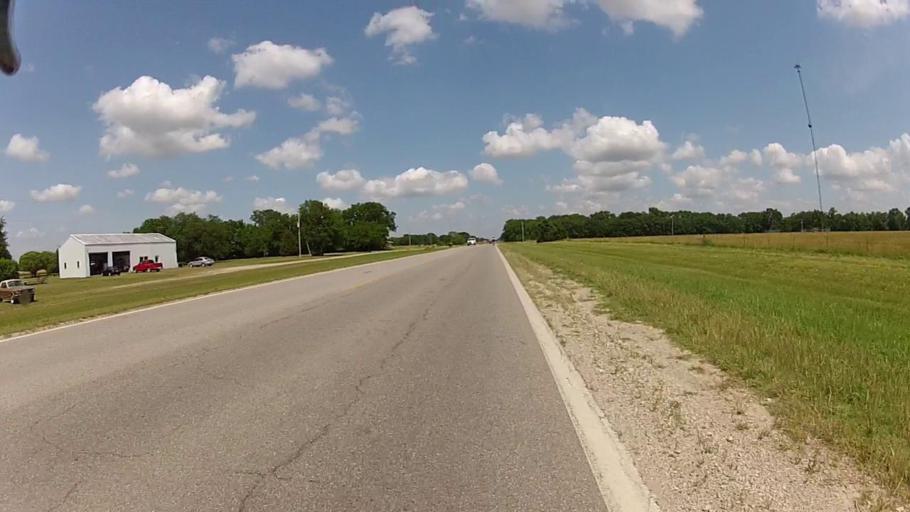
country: US
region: Kansas
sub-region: Labette County
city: Altamont
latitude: 37.1928
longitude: -95.2783
